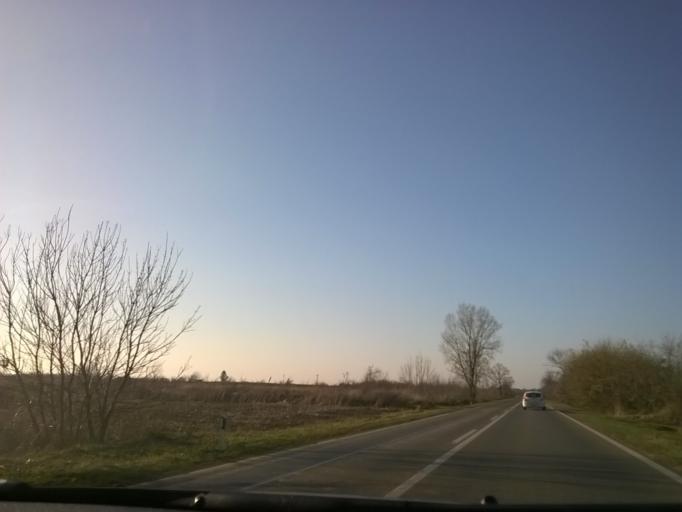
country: RS
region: Autonomna Pokrajina Vojvodina
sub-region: Juznobanatski Okrug
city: Alibunar
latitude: 45.0656
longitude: 20.9744
